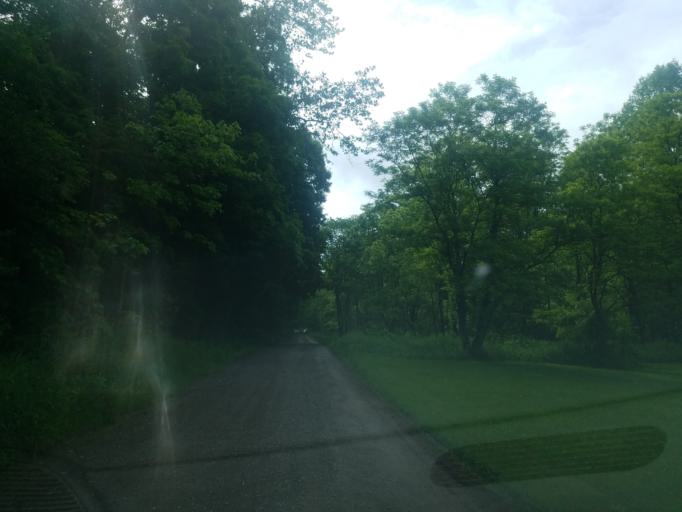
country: US
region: Ohio
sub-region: Holmes County
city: Millersburg
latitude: 40.5218
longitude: -81.8874
